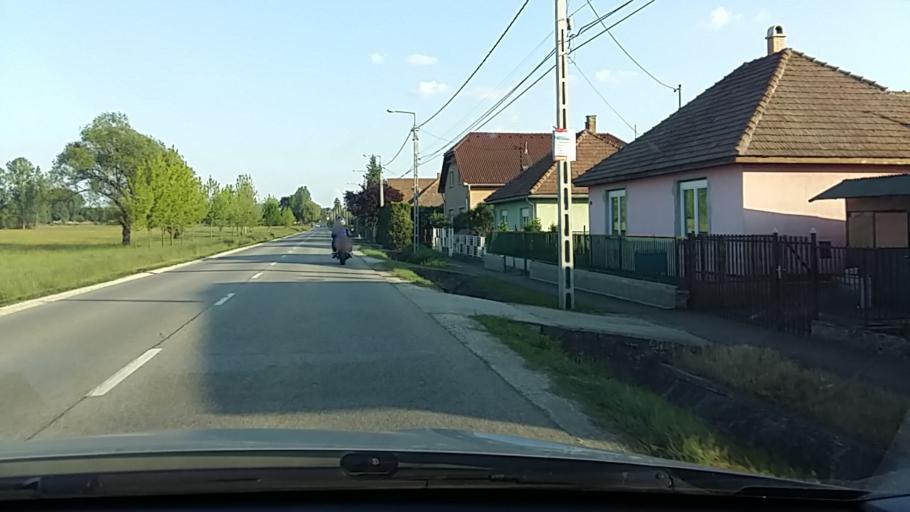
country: HU
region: Pest
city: Orbottyan
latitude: 47.7179
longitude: 19.2316
